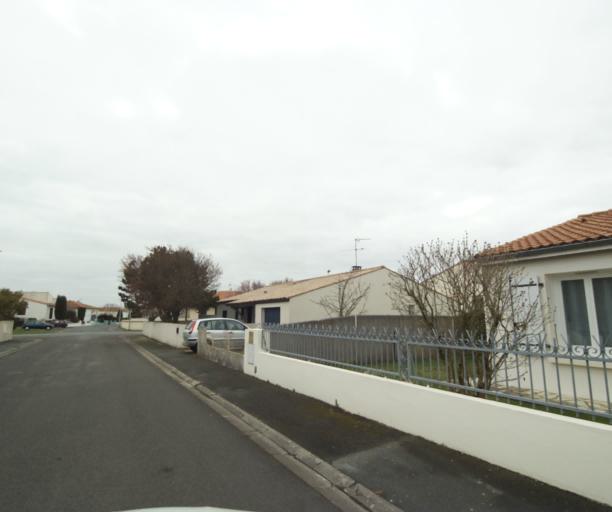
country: FR
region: Poitou-Charentes
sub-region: Departement de la Charente-Maritime
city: Lagord
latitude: 46.1875
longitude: -1.1534
